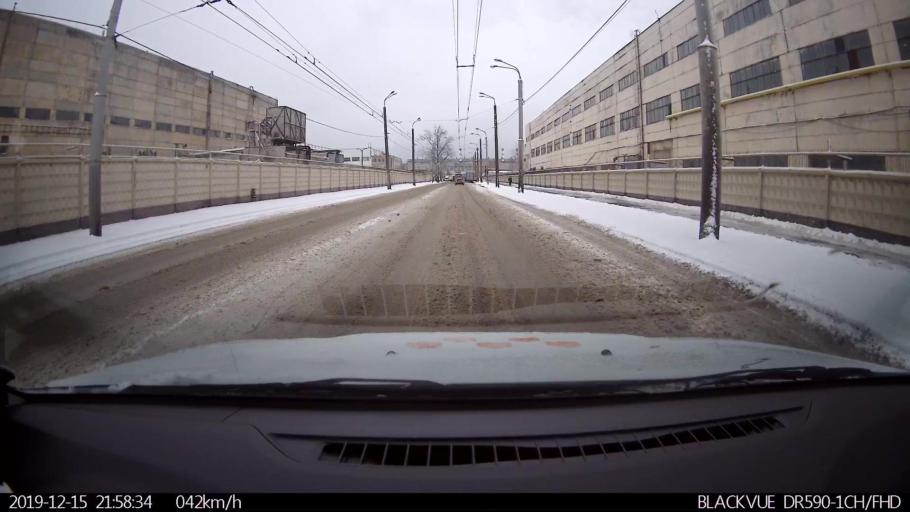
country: RU
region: Nizjnij Novgorod
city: Nizhniy Novgorod
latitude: 56.2473
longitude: 43.9124
